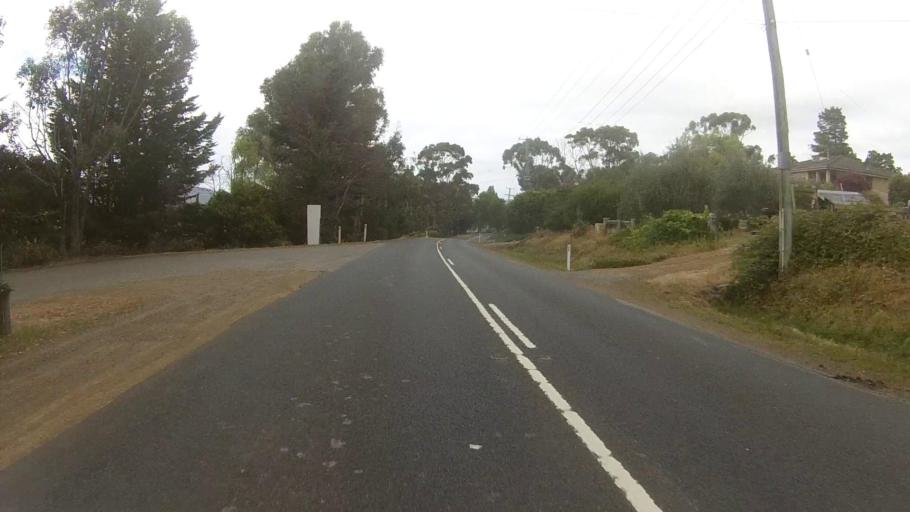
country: AU
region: Tasmania
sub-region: Kingborough
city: Margate
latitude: -43.0170
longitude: 147.2523
